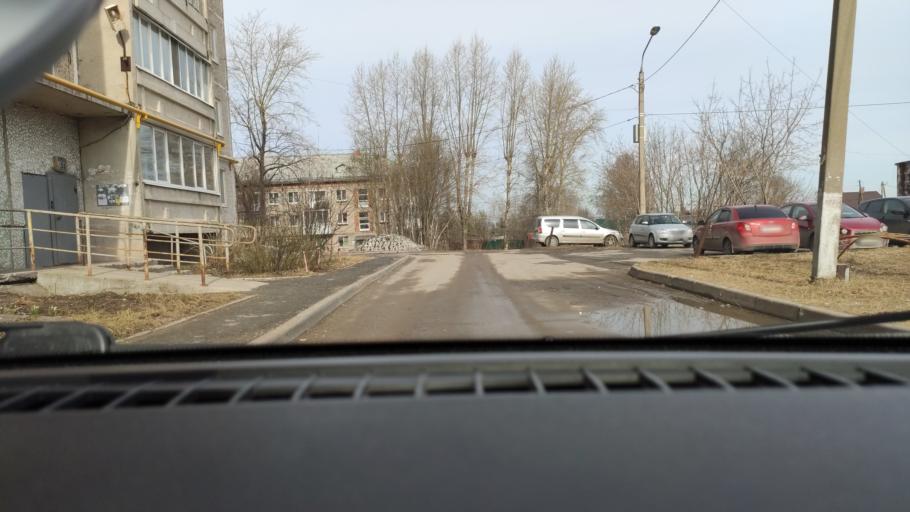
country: RU
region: Perm
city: Perm
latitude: 58.0897
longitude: 56.3936
